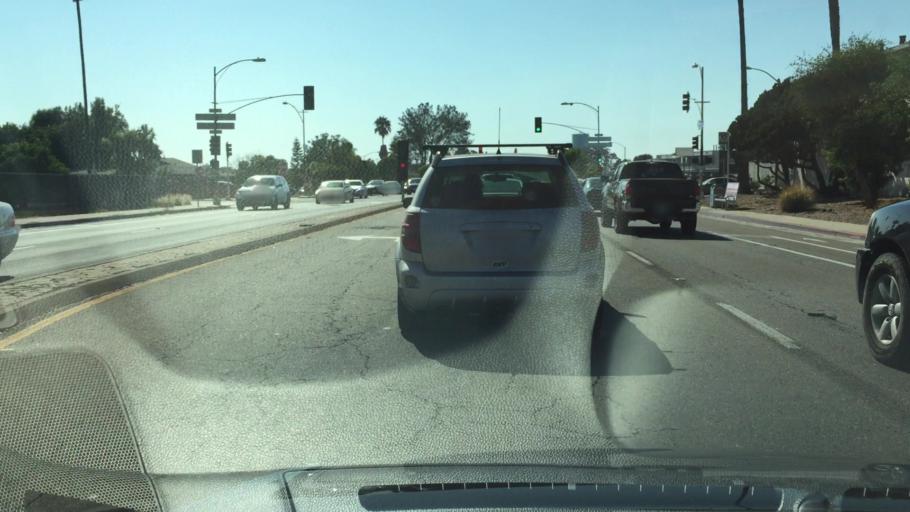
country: US
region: California
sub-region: San Diego County
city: Lemon Grove
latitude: 32.7456
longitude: -117.0580
